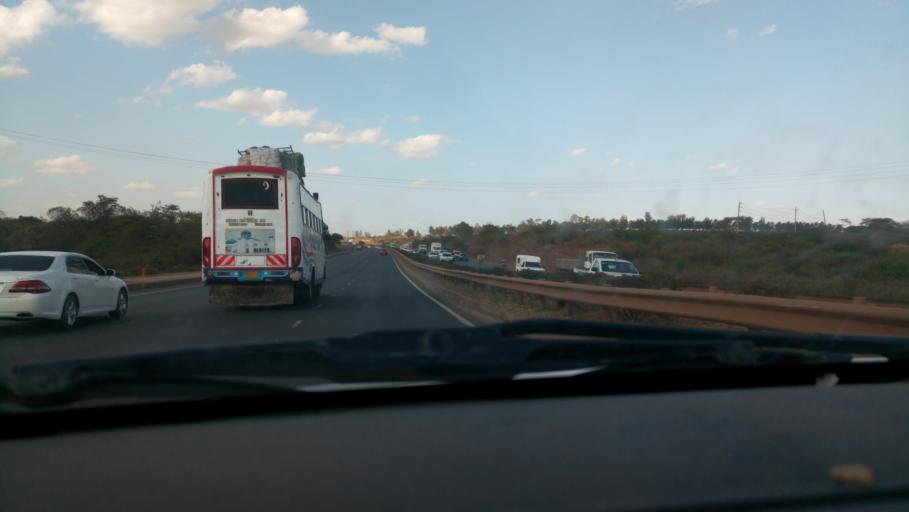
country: KE
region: Nairobi Area
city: Thika
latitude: -1.0875
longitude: 37.0370
